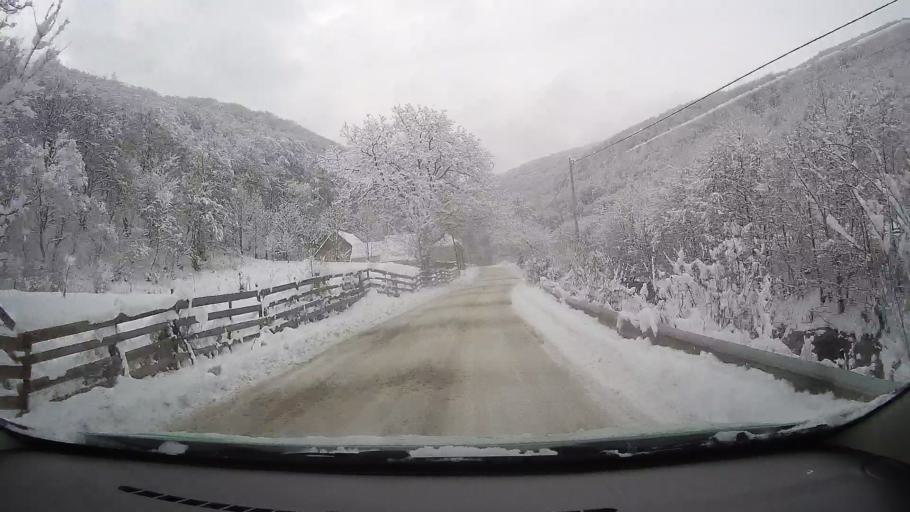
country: RO
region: Alba
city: Pianu de Sus
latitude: 45.8759
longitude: 23.4925
